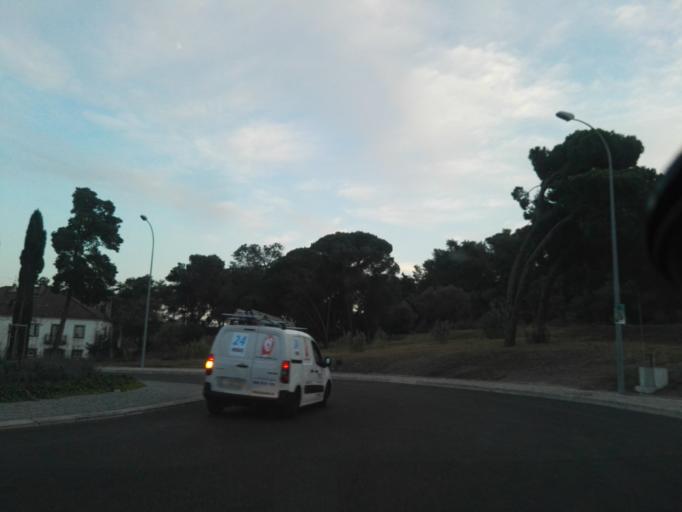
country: PT
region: Lisbon
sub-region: Oeiras
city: Linda-a-Velha
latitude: 38.7028
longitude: -9.2563
